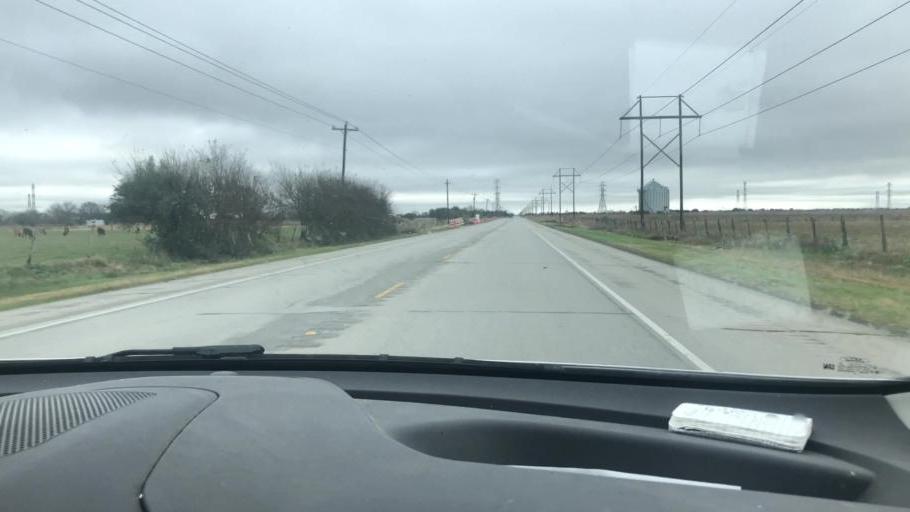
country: US
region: Texas
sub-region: Wharton County
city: Boling
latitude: 29.1808
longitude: -96.0084
